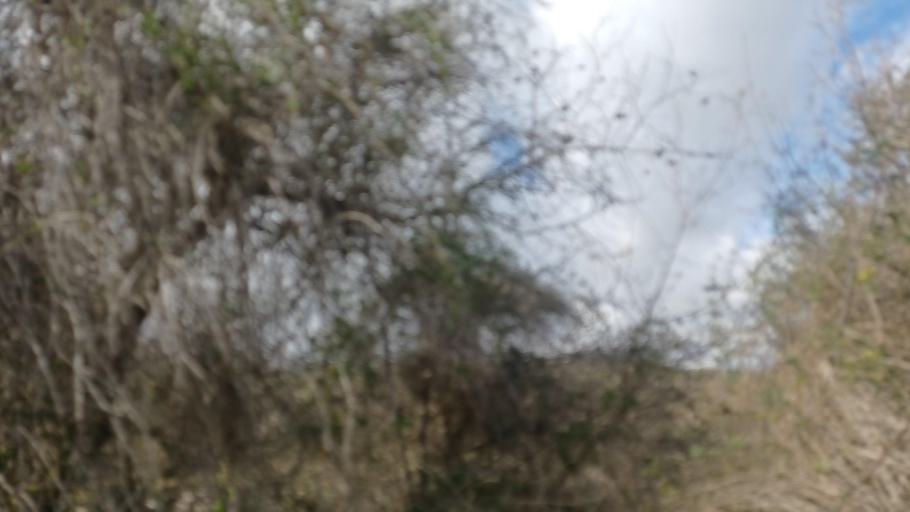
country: CY
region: Pafos
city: Polis
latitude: 34.9640
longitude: 32.4295
